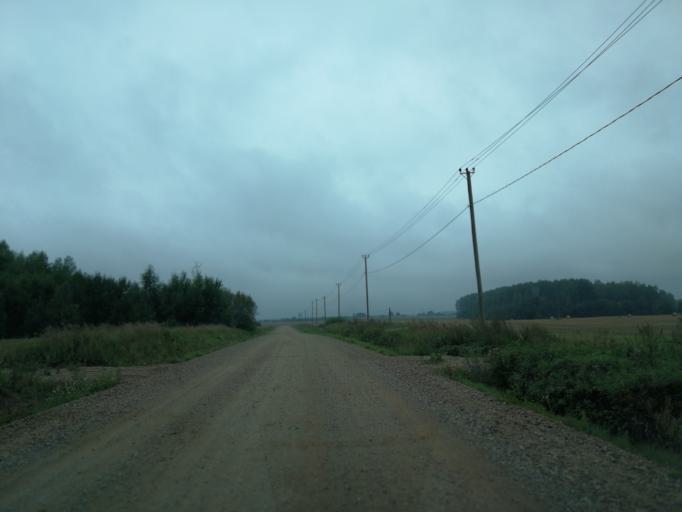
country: LV
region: Vilanu
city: Vilani
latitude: 56.3763
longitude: 27.0480
